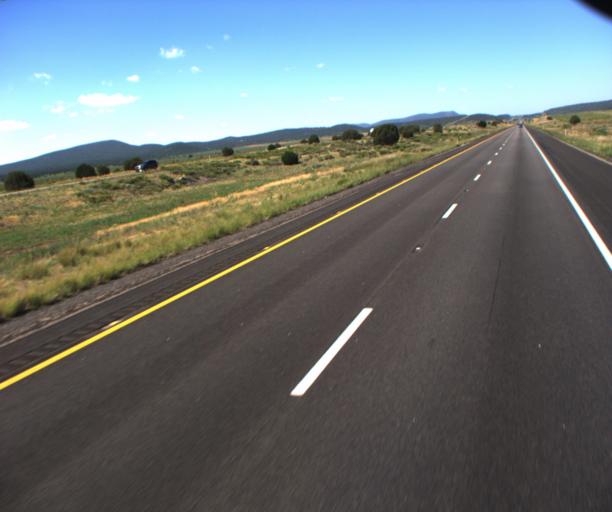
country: US
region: Arizona
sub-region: Mohave County
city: Peach Springs
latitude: 35.2692
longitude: -113.1478
